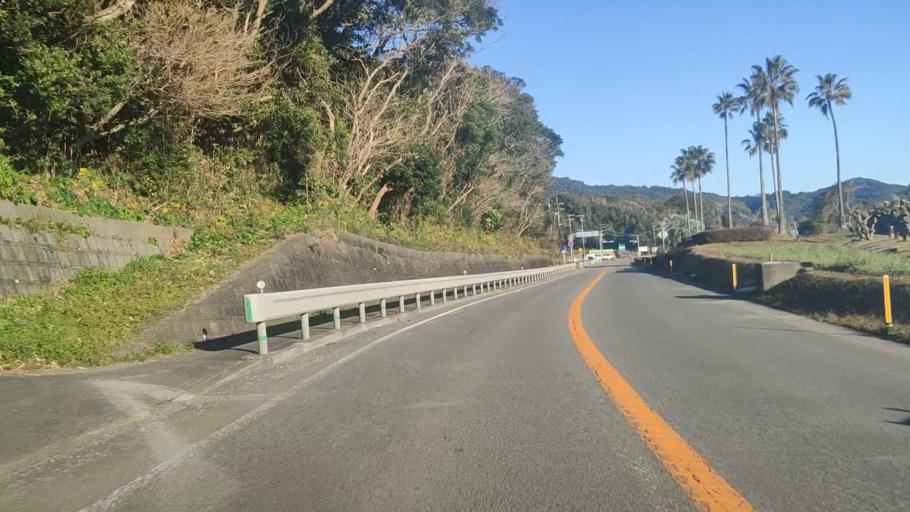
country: JP
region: Miyazaki
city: Nobeoka
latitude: 32.3544
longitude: 131.6211
